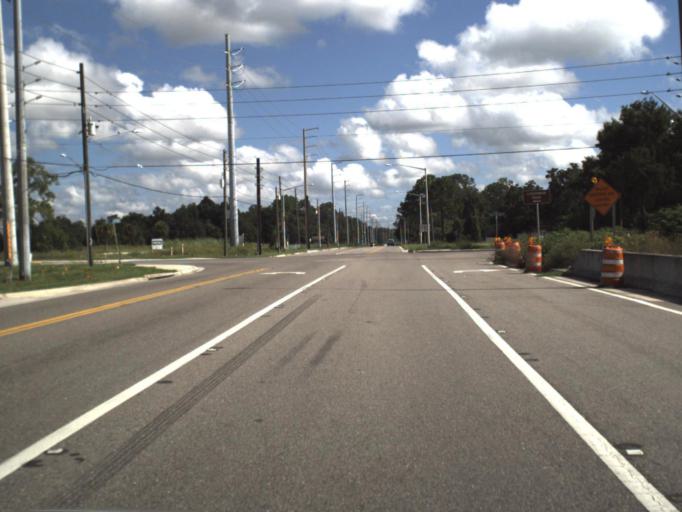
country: US
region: Florida
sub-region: Polk County
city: Loughman
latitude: 28.2364
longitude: -81.5594
